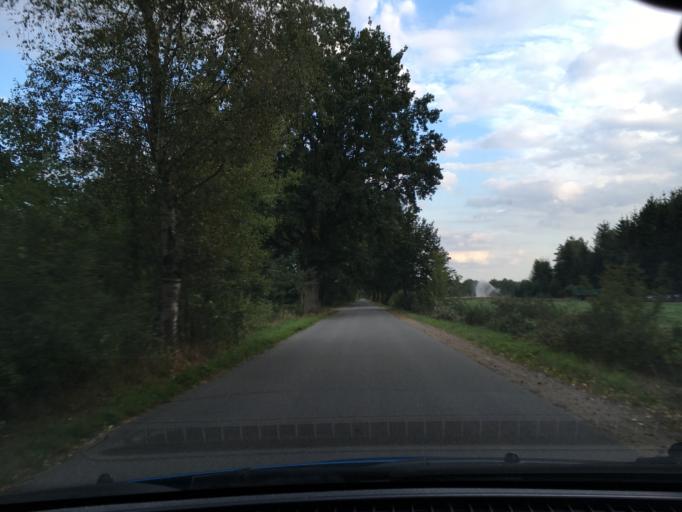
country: DE
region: Lower Saxony
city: Garstedt
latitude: 53.2795
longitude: 10.1882
